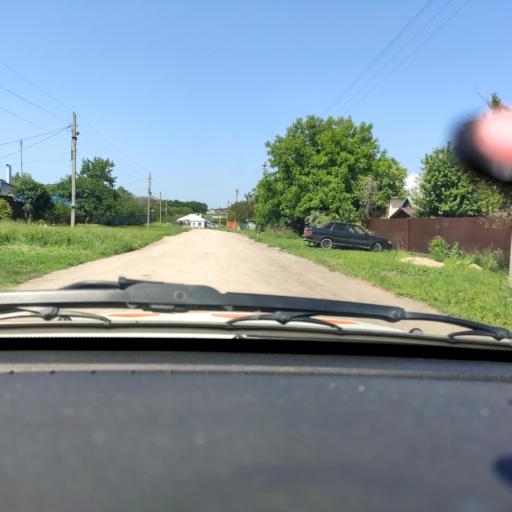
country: RU
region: Voronezj
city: Devitsa
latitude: 51.5961
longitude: 38.9879
